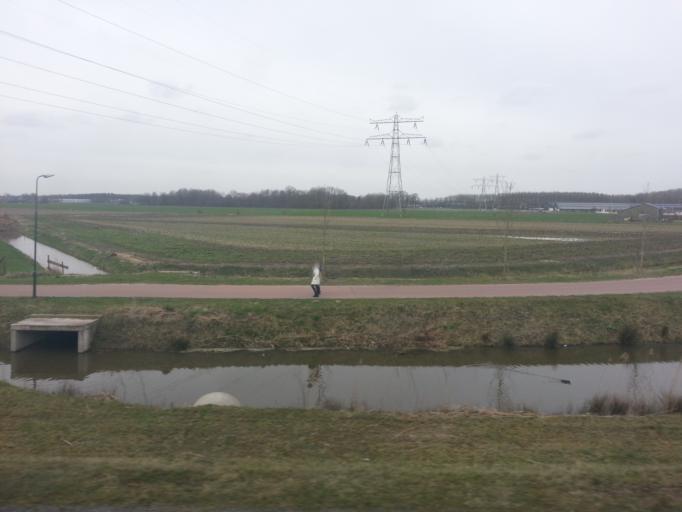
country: NL
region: Utrecht
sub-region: Gemeente Utrecht
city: Lunetten
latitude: 52.0519
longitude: 5.1561
